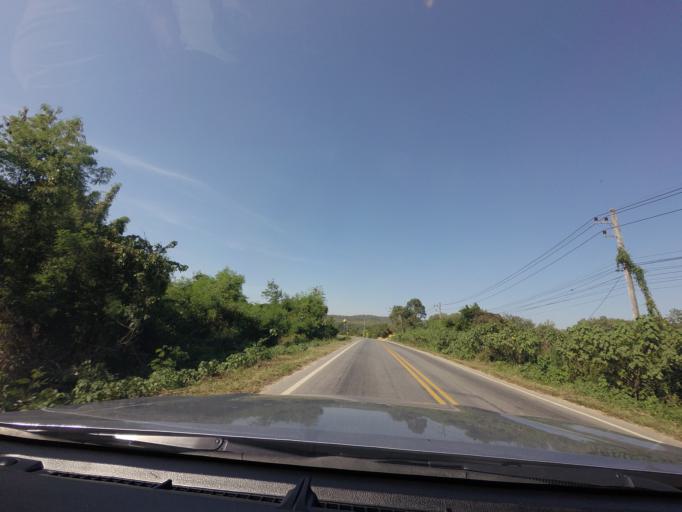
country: TH
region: Sukhothai
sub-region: Amphoe Si Satchanalai
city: Si Satchanalai
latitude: 17.6273
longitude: 99.7011
